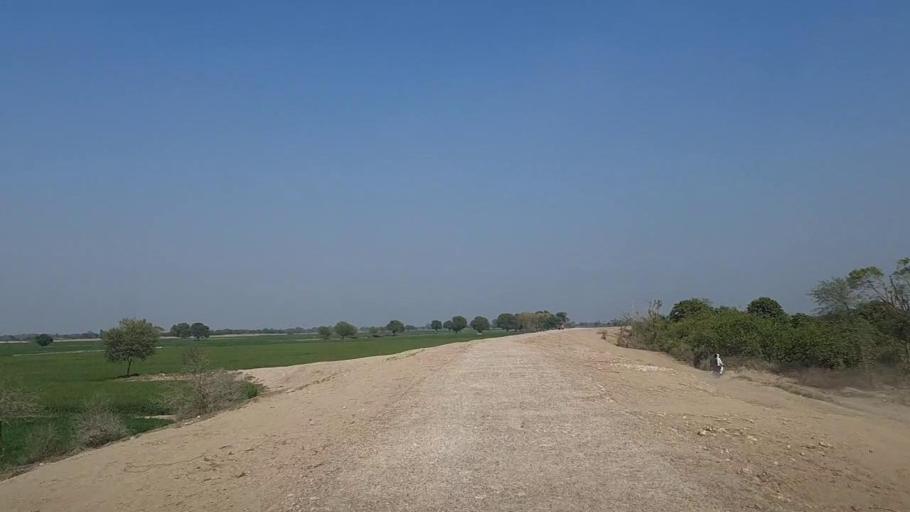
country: PK
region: Sindh
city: Moro
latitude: 26.7947
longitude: 67.9375
